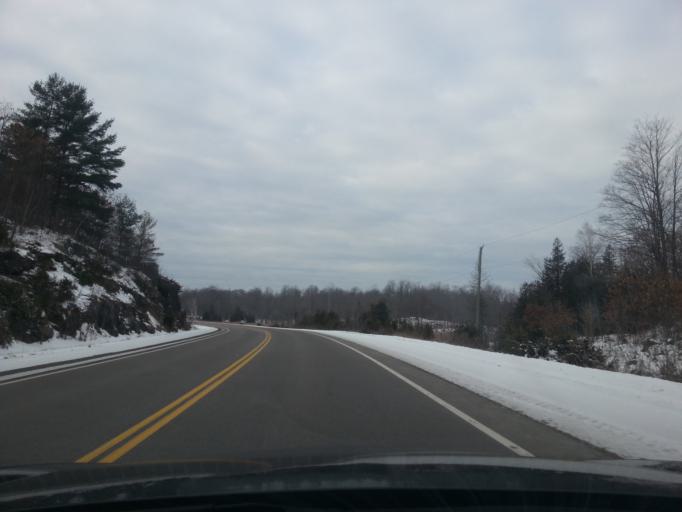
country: CA
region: Ontario
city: Perth
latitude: 44.7943
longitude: -76.6996
